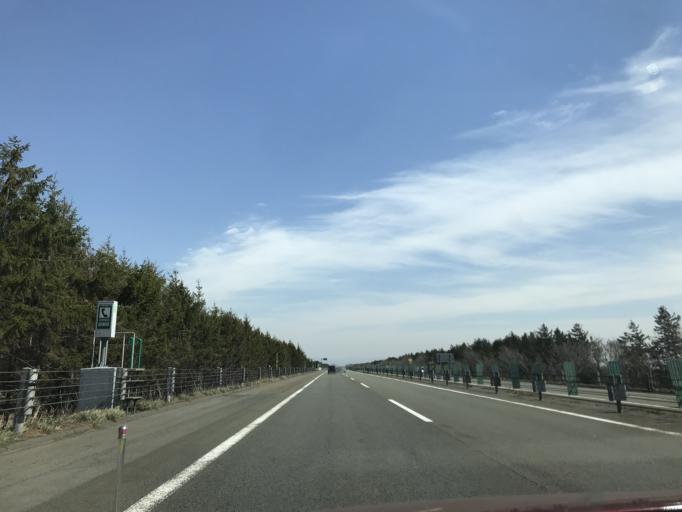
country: JP
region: Hokkaido
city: Ebetsu
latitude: 43.1240
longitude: 141.6366
